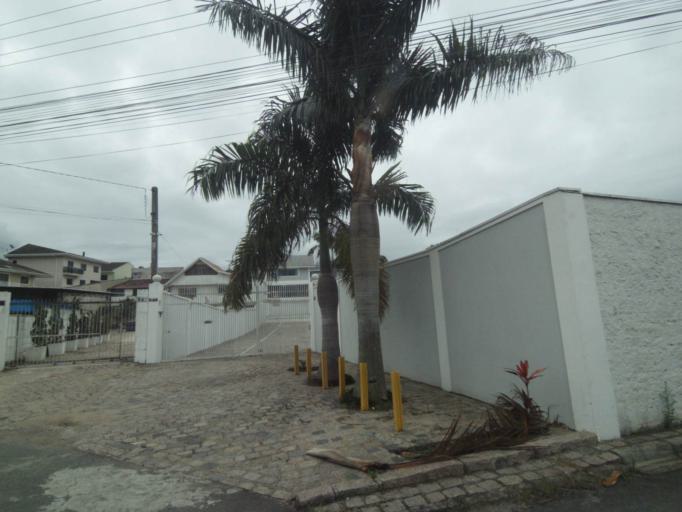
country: BR
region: Parana
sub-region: Curitiba
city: Curitiba
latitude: -25.4909
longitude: -49.2839
